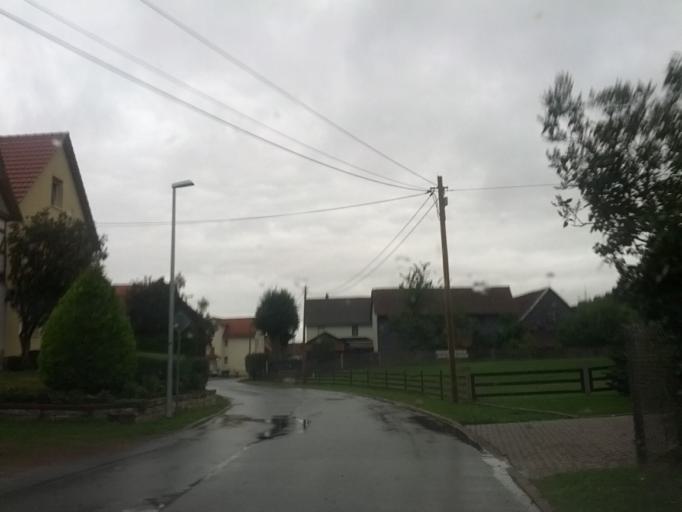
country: DE
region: Thuringia
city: Mechterstadt
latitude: 50.9279
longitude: 10.4796
